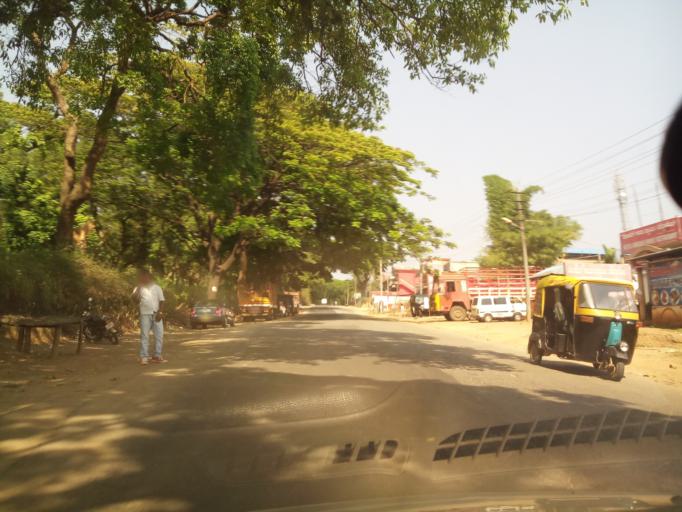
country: IN
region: Karnataka
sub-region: Hassan
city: Sakleshpur
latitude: 12.9486
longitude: 75.8035
